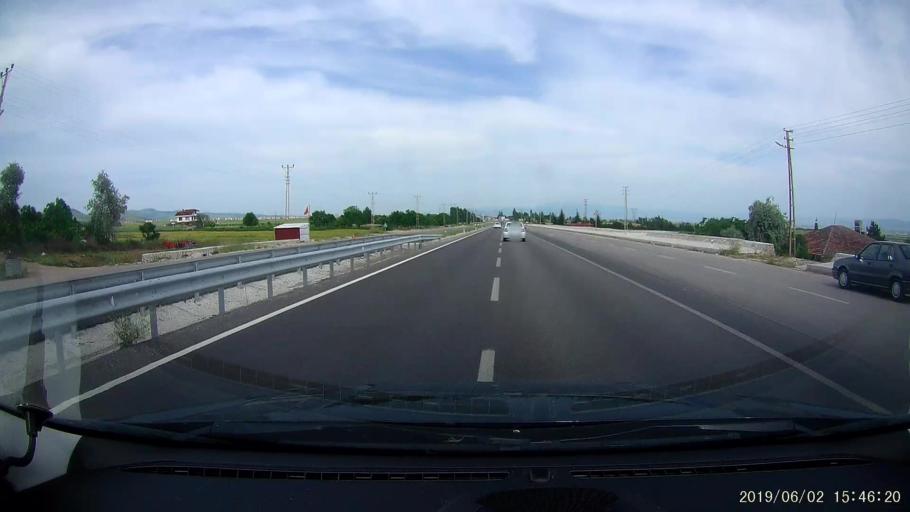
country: TR
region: Amasya
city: Merzifon
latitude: 40.8631
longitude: 35.4005
